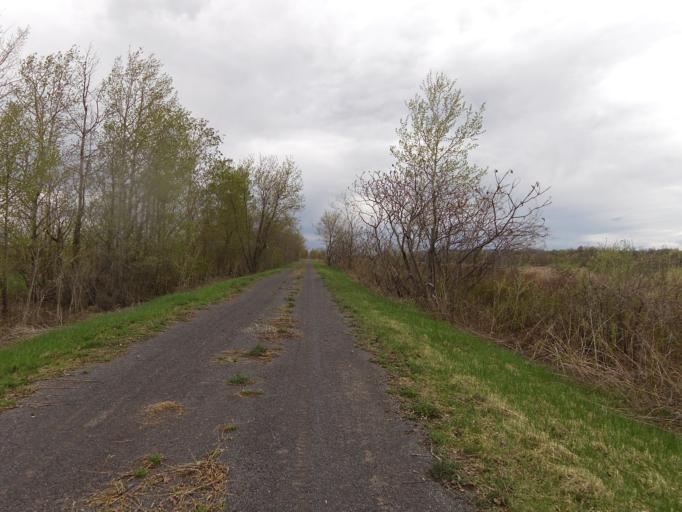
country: CA
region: Quebec
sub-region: Outaouais
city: Papineauville
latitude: 45.5248
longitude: -74.9047
